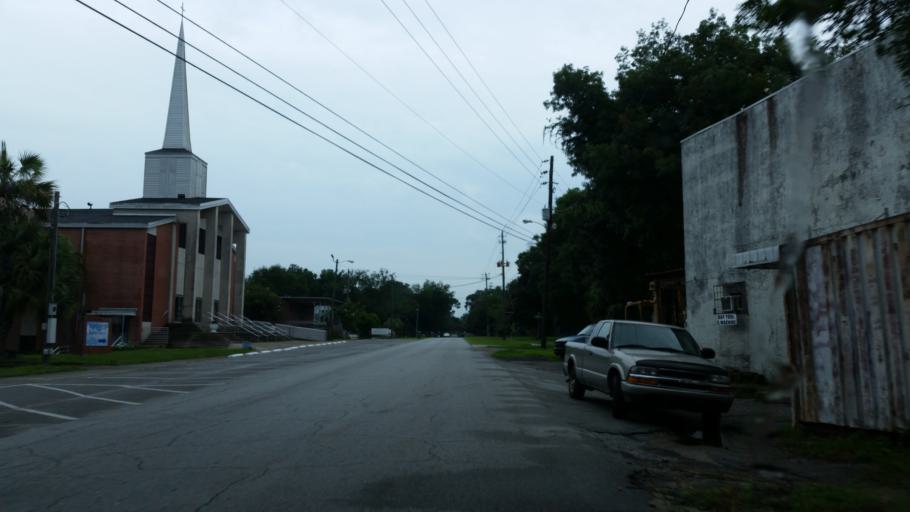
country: US
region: Florida
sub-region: Escambia County
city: Warrington
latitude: 30.3858
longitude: -87.2792
